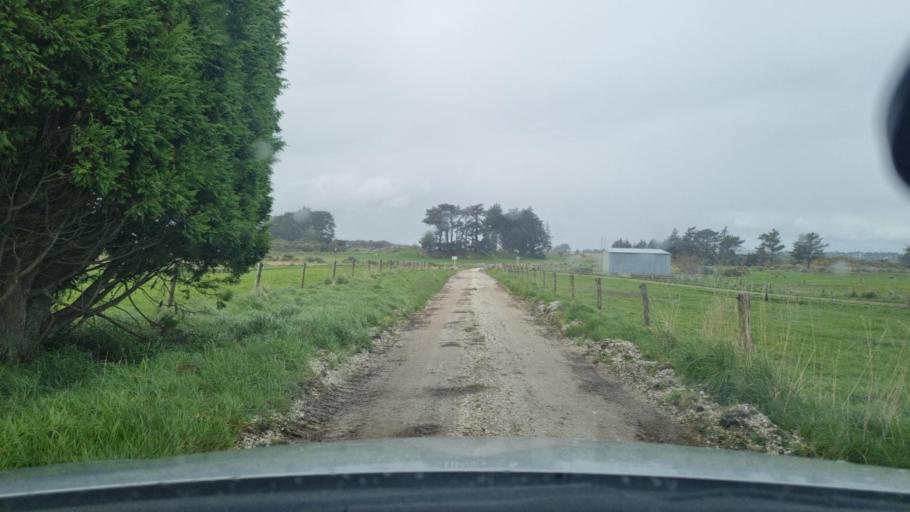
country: NZ
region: Southland
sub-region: Invercargill City
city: Bluff
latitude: -46.5122
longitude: 168.4099
